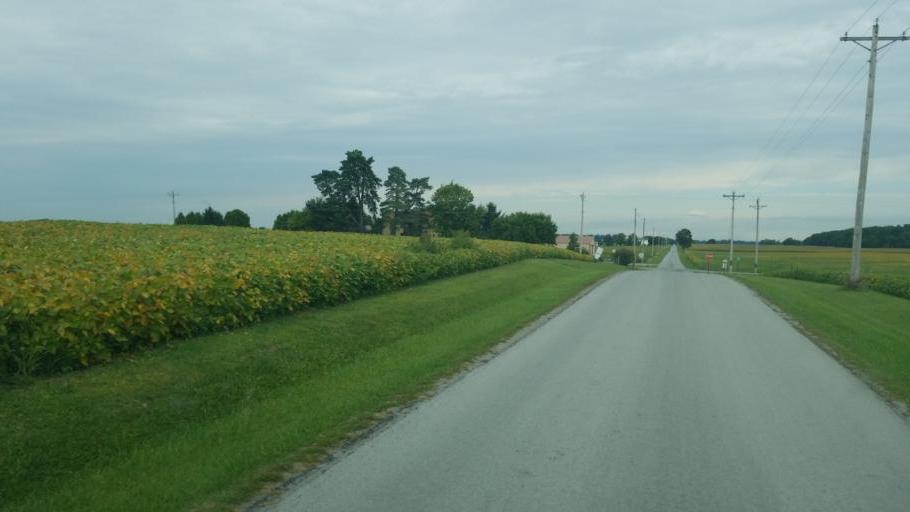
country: US
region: Ohio
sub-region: Wyandot County
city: Upper Sandusky
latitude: 40.7882
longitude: -83.1884
